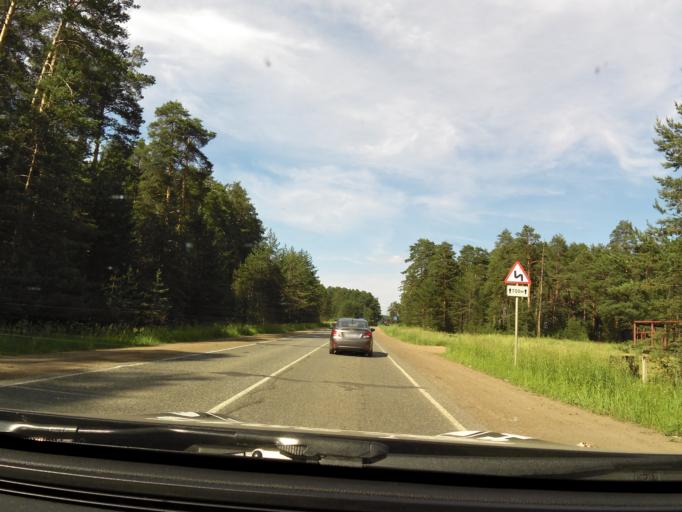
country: RU
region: Kirov
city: Belaya Kholunitsa
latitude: 58.8577
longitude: 50.8407
